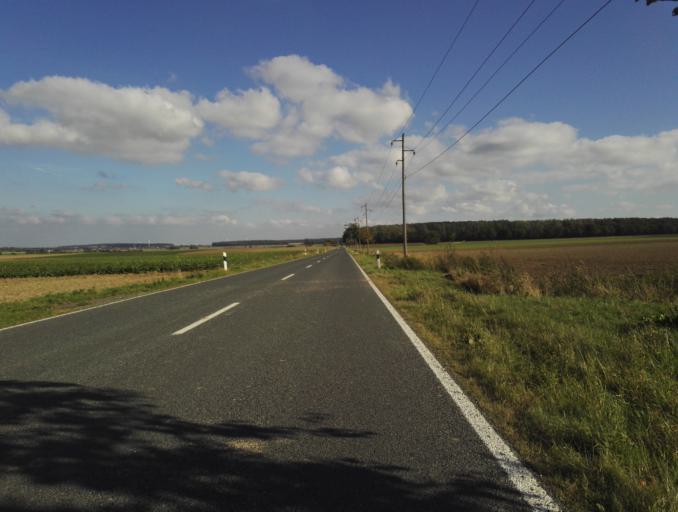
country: DE
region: Lower Saxony
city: Schellerten
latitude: 52.1501
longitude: 10.0947
